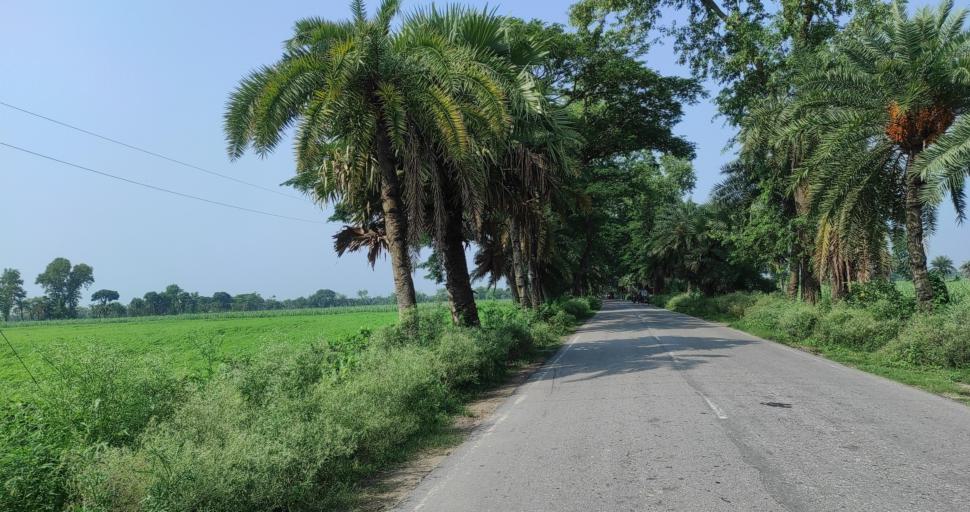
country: BD
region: Rajshahi
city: Ishurdi
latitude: 24.2699
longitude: 89.0540
